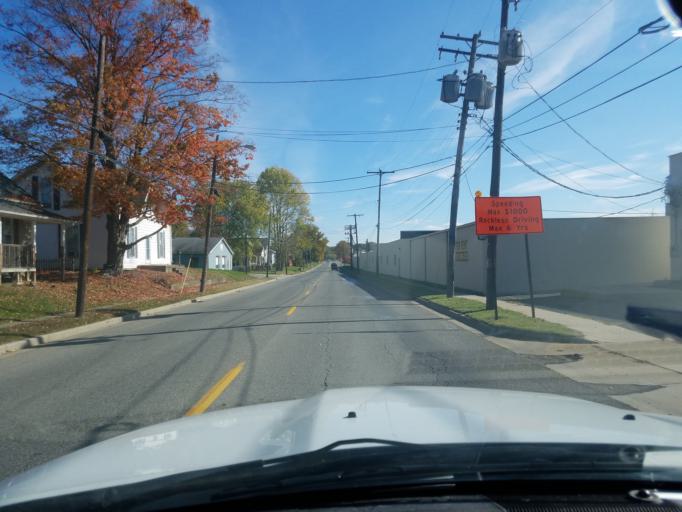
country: US
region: Indiana
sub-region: Jennings County
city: North Vernon
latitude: 39.0056
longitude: -85.6207
